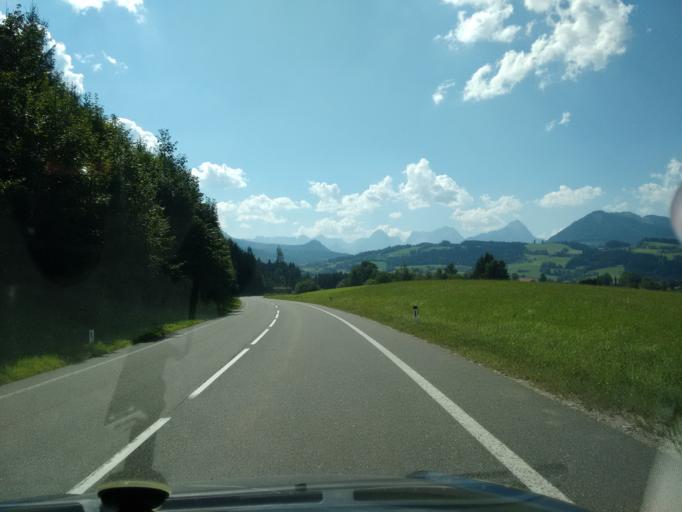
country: AT
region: Upper Austria
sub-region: Politischer Bezirk Kirchdorf an der Krems
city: Rossleithen
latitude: 47.7146
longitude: 14.3242
